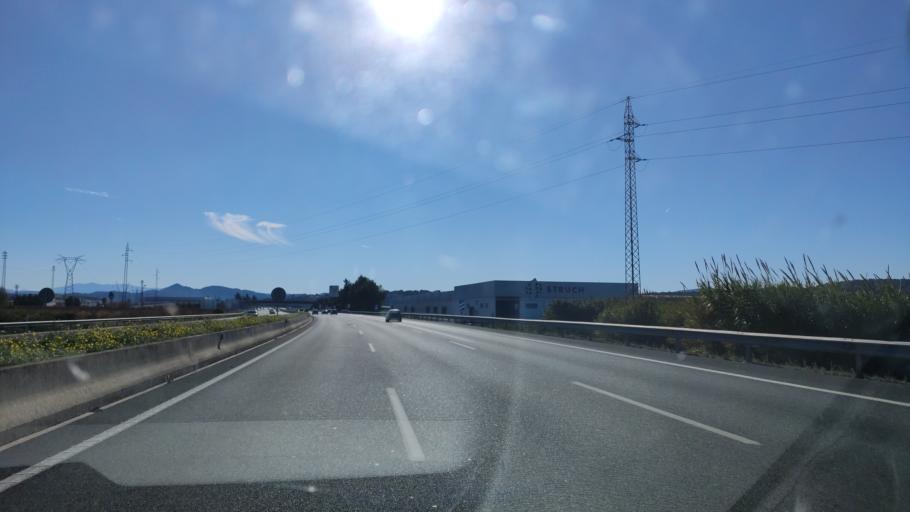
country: ES
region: Valencia
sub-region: Provincia de Valencia
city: Alberic
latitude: 39.1239
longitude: -0.5307
